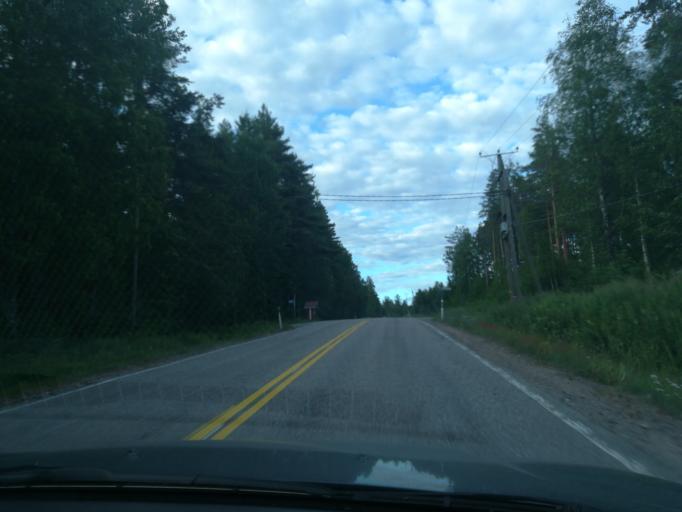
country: FI
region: Southern Savonia
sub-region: Mikkeli
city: Puumala
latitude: 61.5679
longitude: 28.1243
